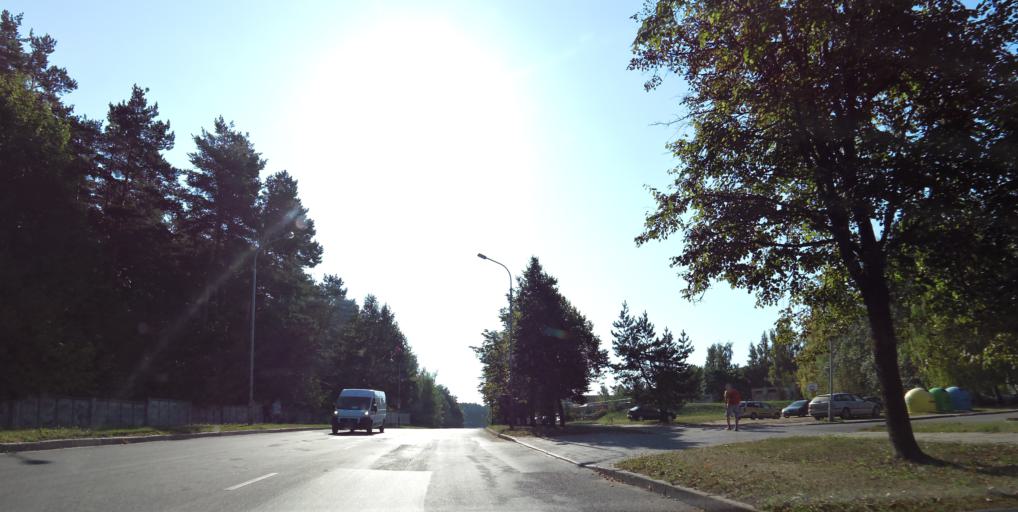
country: LT
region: Vilnius County
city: Justiniskes
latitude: 54.7070
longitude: 25.2293
